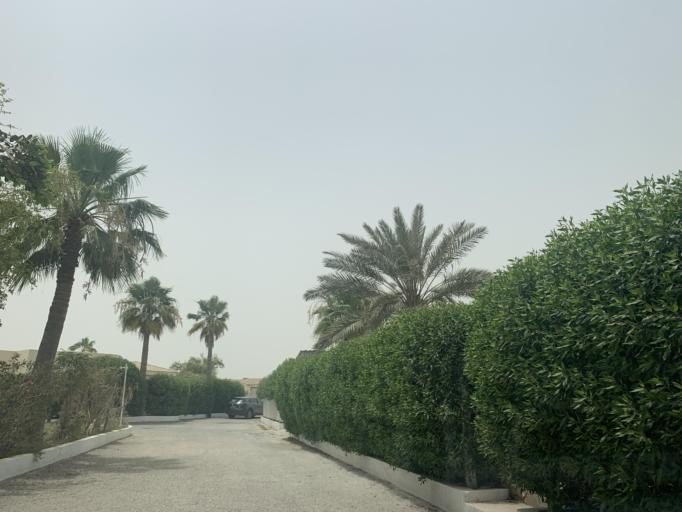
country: BH
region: Manama
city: Jidd Hafs
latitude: 26.2285
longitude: 50.5193
